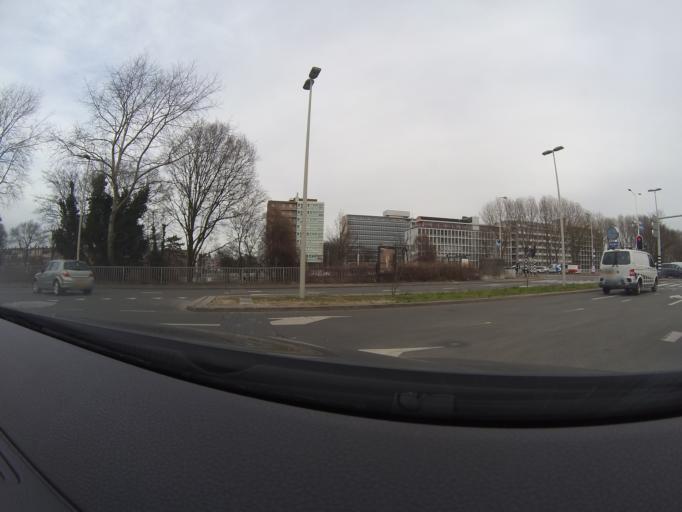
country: NL
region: South Holland
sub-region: Gemeente Den Haag
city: Scheveningen
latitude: 52.0853
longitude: 4.2722
